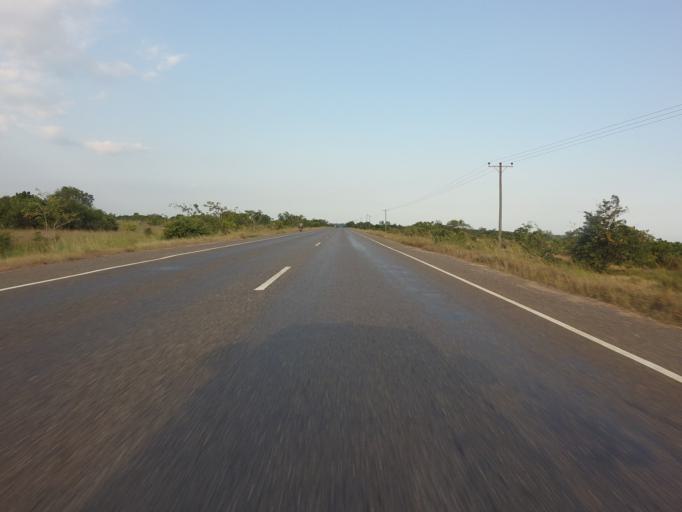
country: GH
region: Volta
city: Anloga
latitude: 6.0800
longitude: 0.5803
